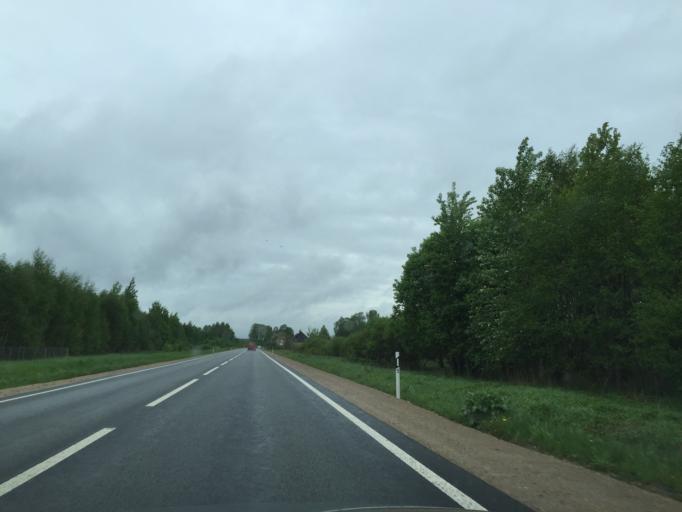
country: LV
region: Ogre
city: Jumprava
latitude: 56.6490
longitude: 24.9017
